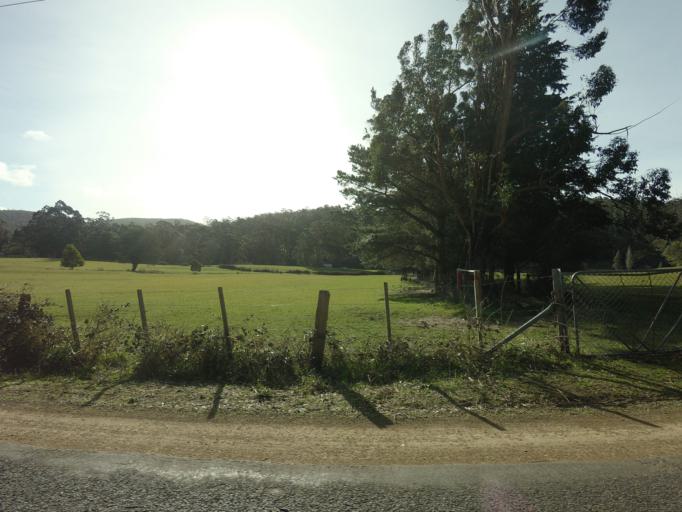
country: AU
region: Tasmania
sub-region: Kingborough
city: Kettering
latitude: -43.1086
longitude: 147.2508
